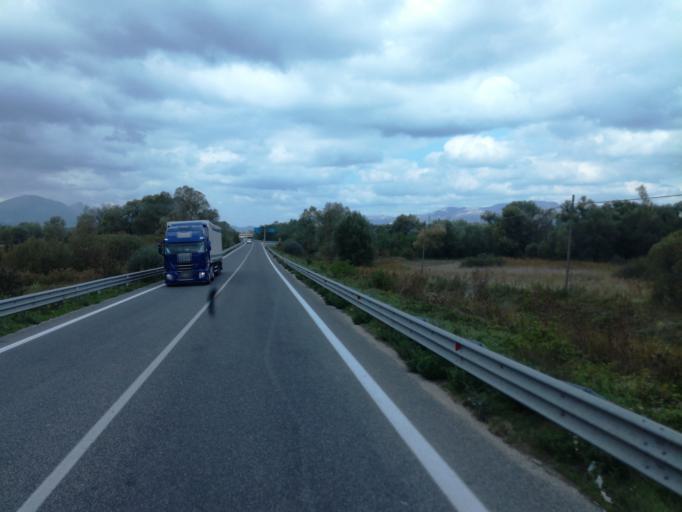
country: IT
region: Molise
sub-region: Provincia di Campobasso
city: San Polomatese
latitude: 41.4824
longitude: 14.4954
